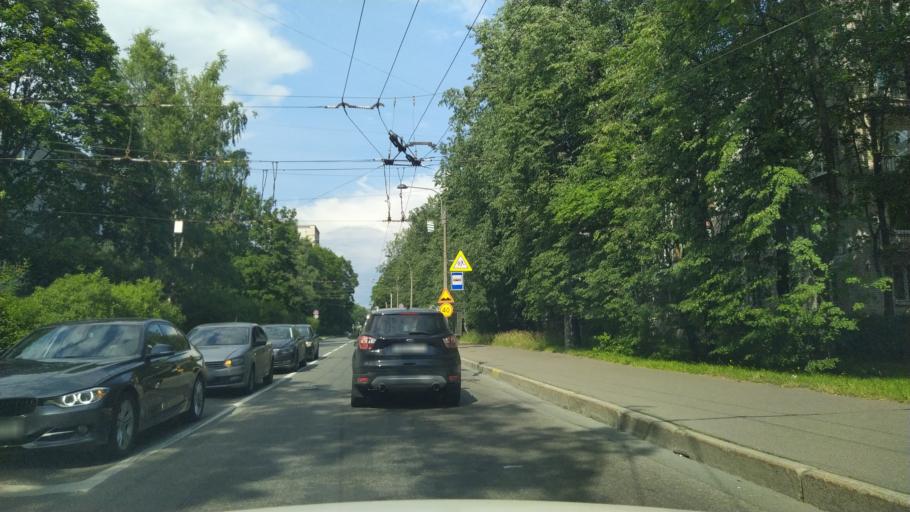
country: RU
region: Leningrad
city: Sampsonievskiy
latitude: 59.9960
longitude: 30.3453
